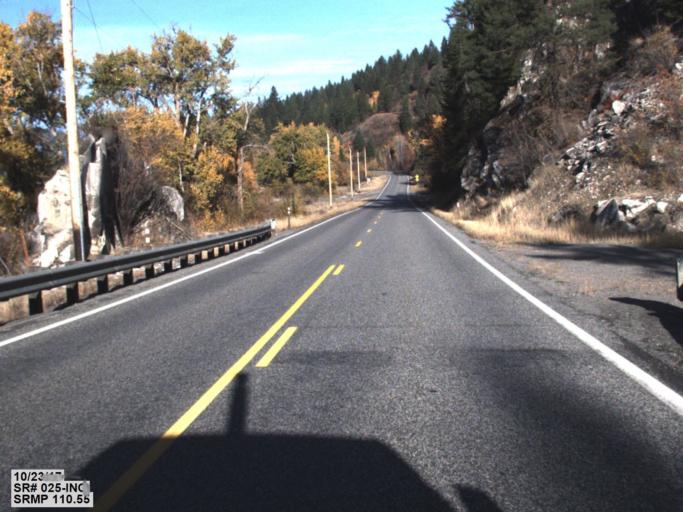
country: CA
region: British Columbia
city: Rossland
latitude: 48.8898
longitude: -117.8248
